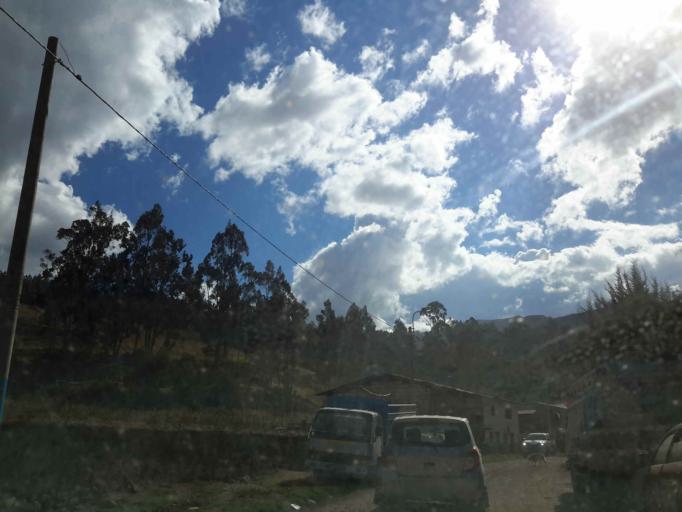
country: PE
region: Apurimac
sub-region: Provincia de Andahuaylas
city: Pacucha
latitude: -13.6150
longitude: -73.3344
